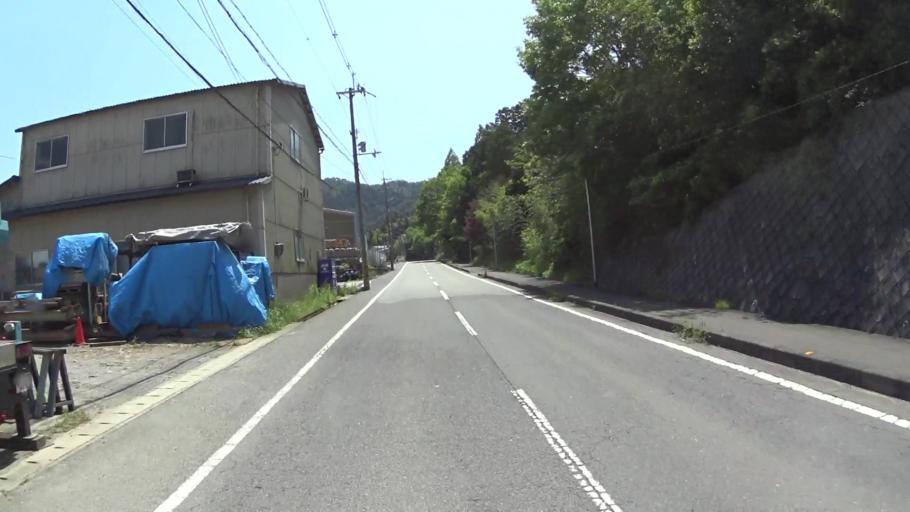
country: JP
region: Kyoto
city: Kameoka
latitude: 35.0337
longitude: 135.4846
